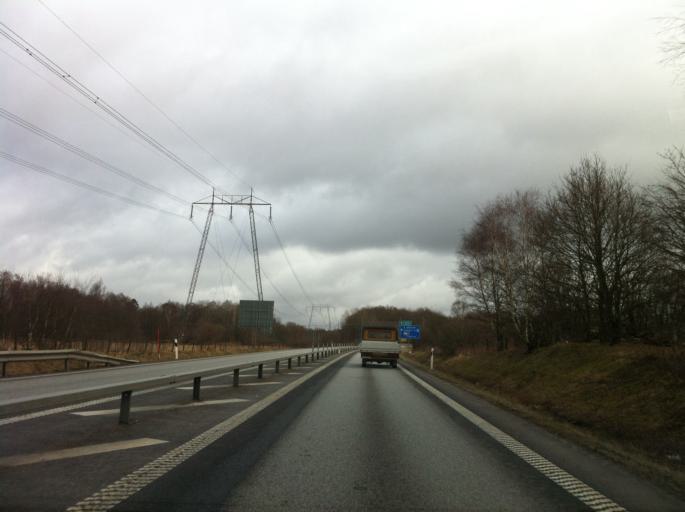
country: SE
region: Skane
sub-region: Hoors Kommun
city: Loberod
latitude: 55.8237
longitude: 13.5271
